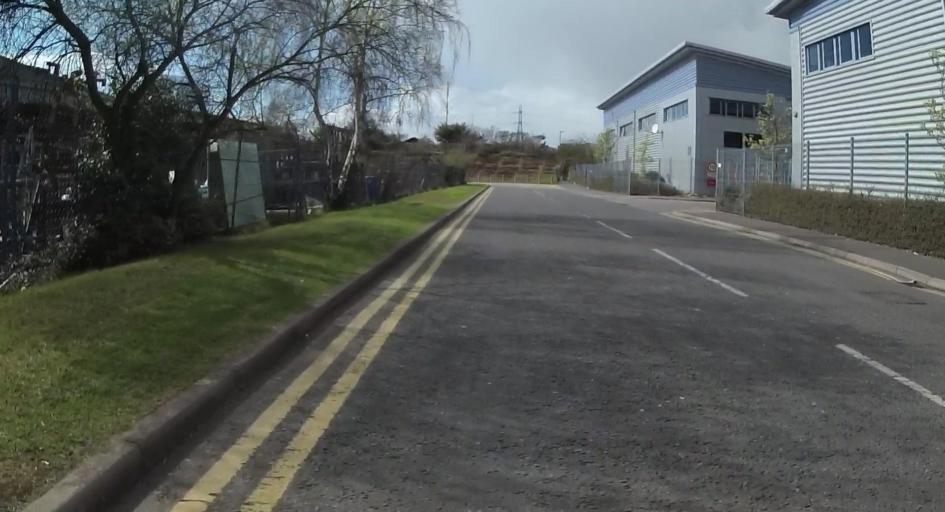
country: GB
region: England
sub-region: Surrey
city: Byfleet
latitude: 51.3480
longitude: -0.4779
